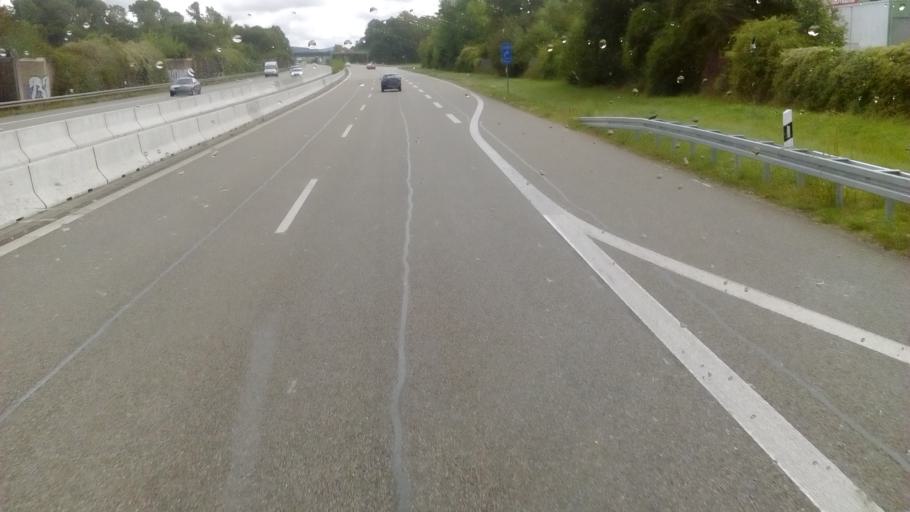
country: FR
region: Alsace
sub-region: Departement du Haut-Rhin
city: Huningue
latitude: 47.6233
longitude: 7.5773
